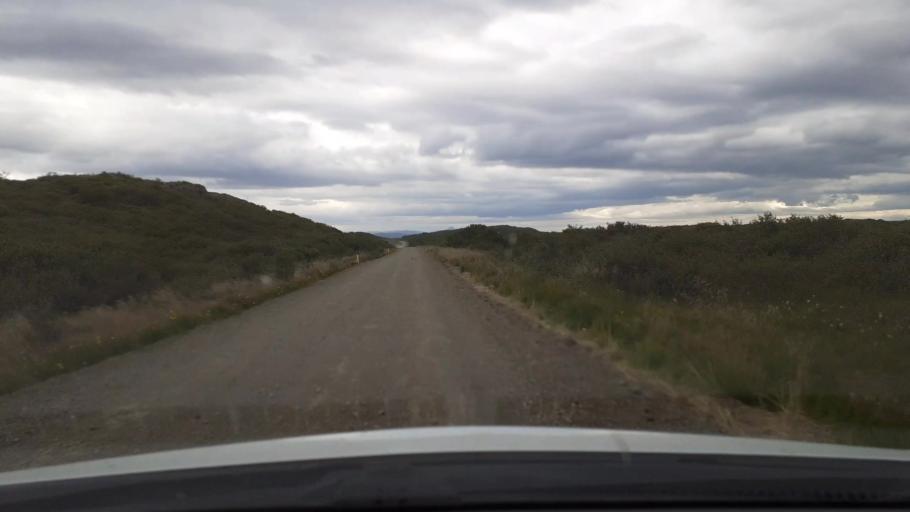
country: IS
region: West
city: Borgarnes
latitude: 64.5959
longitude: -21.9828
